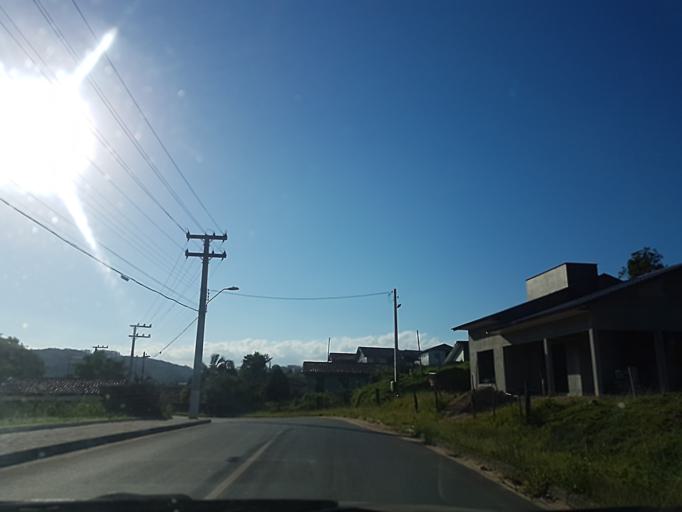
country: BR
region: Santa Catarina
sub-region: Braco Do Norte
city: Braco do Norte
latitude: -28.3300
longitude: -49.1651
